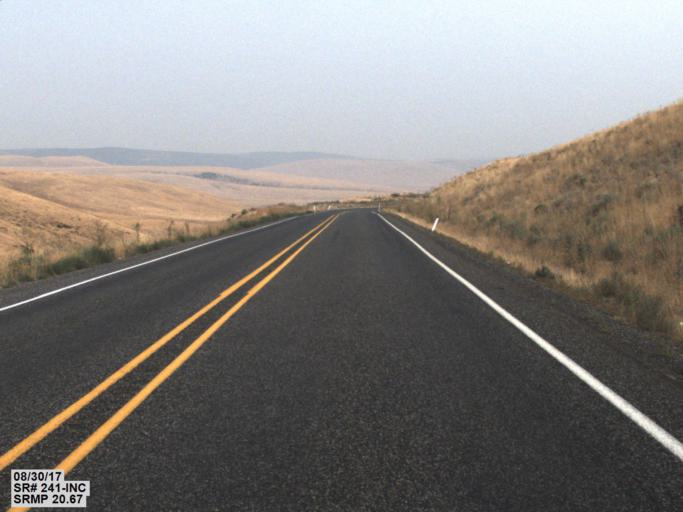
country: US
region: Washington
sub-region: Yakima County
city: Sunnyside
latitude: 46.4843
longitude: -119.9177
